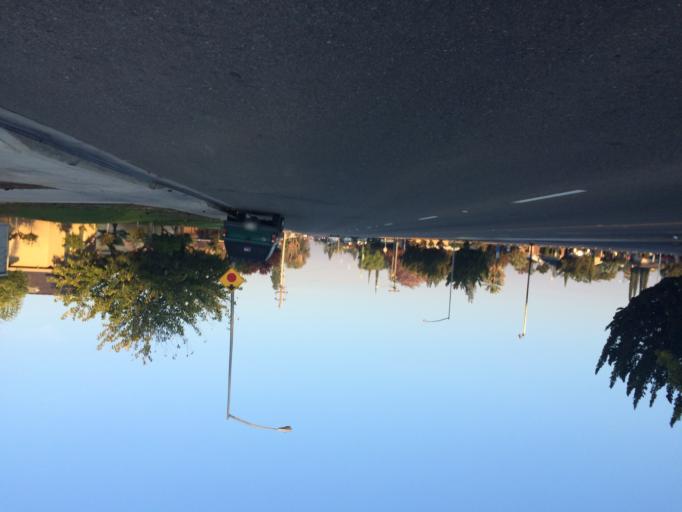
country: US
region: California
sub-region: Fresno County
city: Tarpey Village
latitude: 36.8012
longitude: -119.7213
